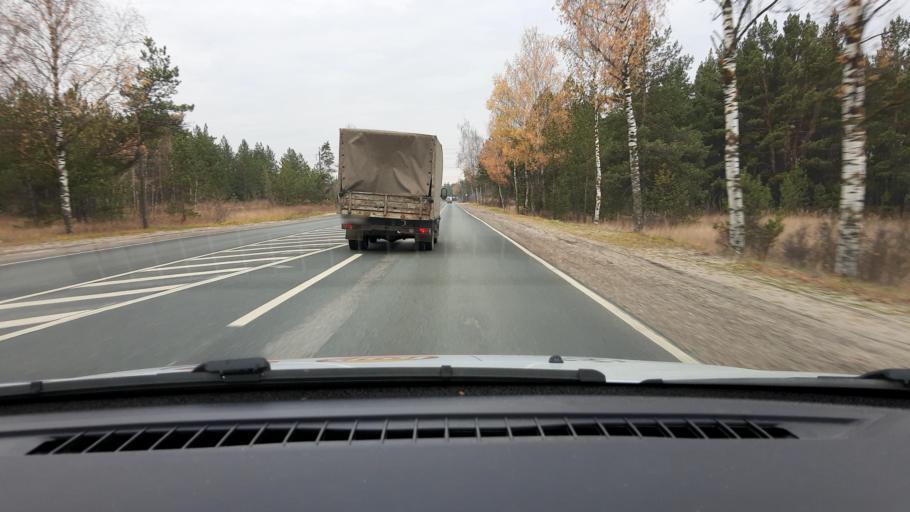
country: RU
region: Nizjnij Novgorod
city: Dzerzhinsk
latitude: 56.2692
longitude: 43.4721
